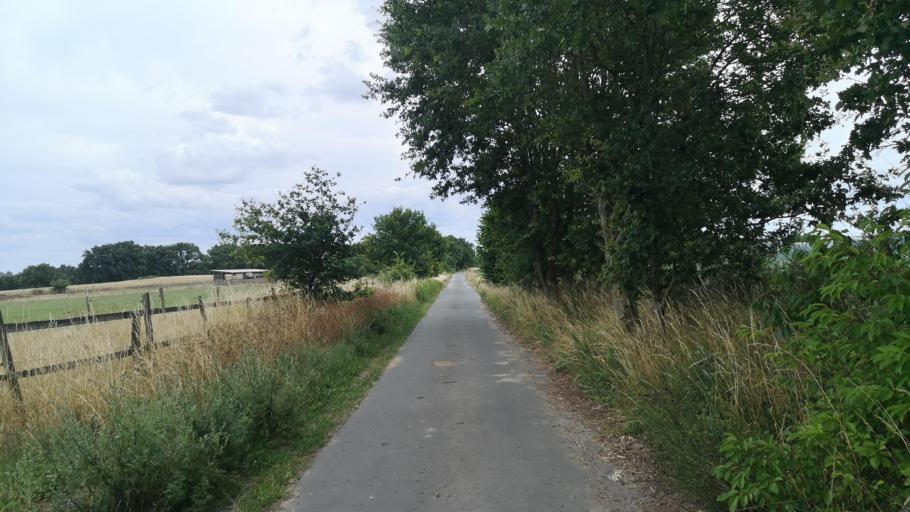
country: DE
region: Lower Saxony
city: Thomasburg
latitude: 53.2298
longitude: 10.6977
